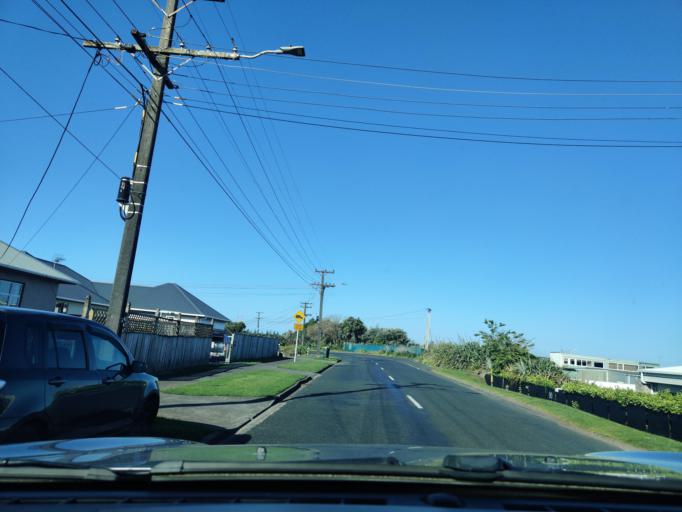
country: NZ
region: Taranaki
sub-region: New Plymouth District
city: New Plymouth
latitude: -39.0469
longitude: 174.1100
